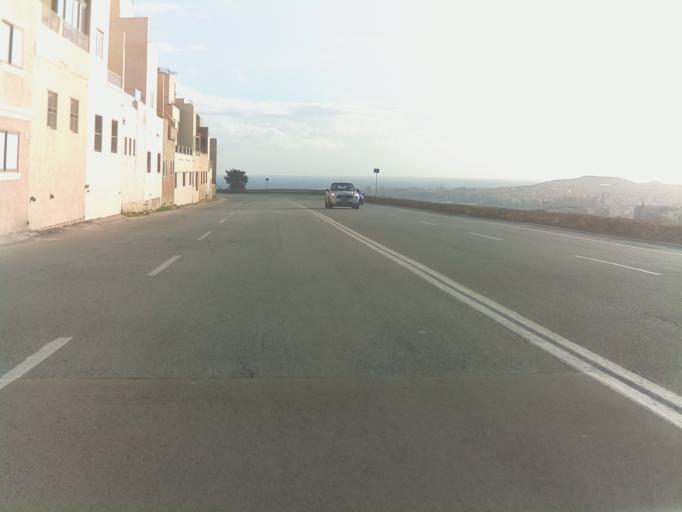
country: MT
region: Il-Mellieha
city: Mellieha
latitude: 35.9530
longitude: 14.3690
